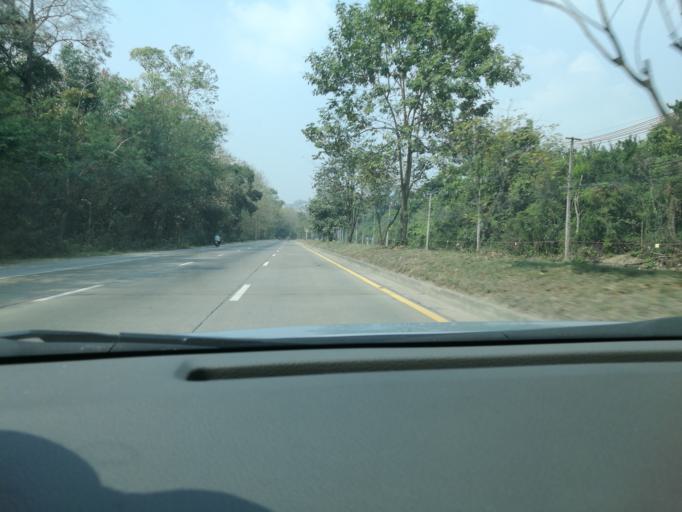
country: TH
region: Sara Buri
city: Chaloem Phra Kiat
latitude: 14.6787
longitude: 100.8784
